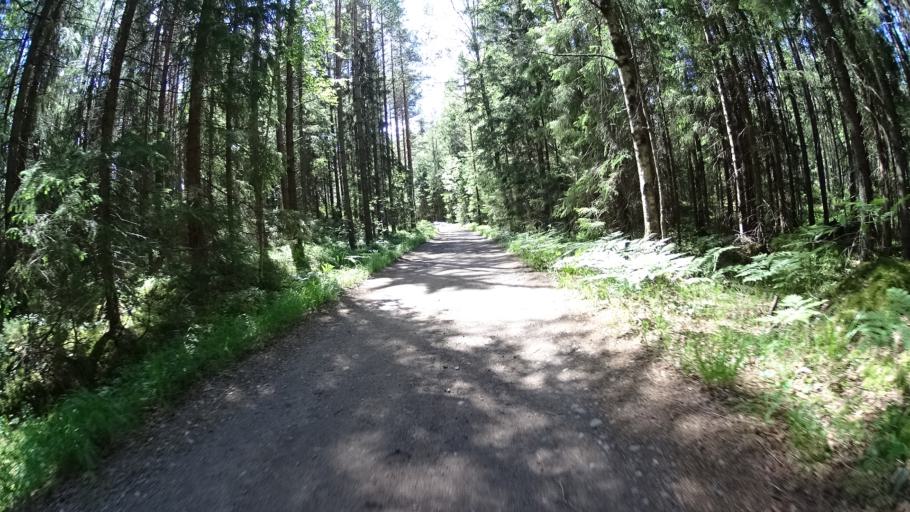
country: FI
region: Uusimaa
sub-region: Helsinki
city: Vihti
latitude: 60.3281
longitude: 24.4785
